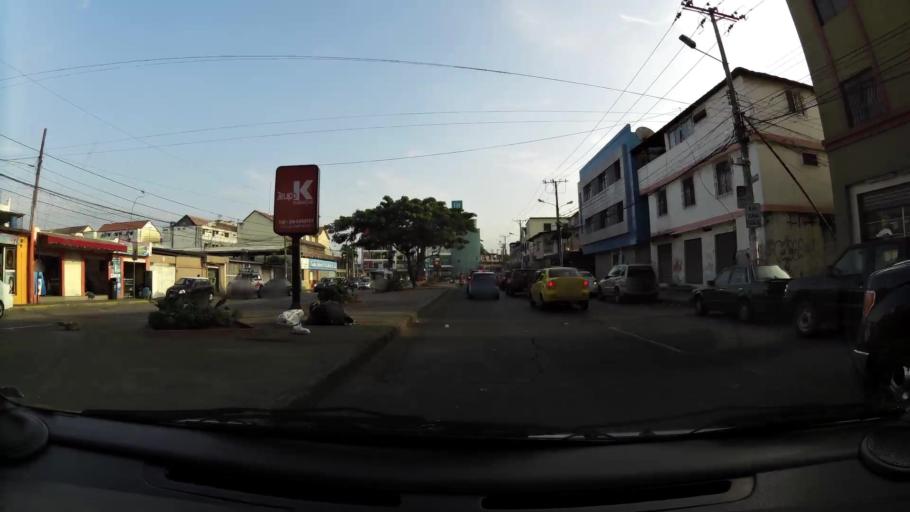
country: EC
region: Guayas
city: Eloy Alfaro
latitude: -2.1324
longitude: -79.9035
